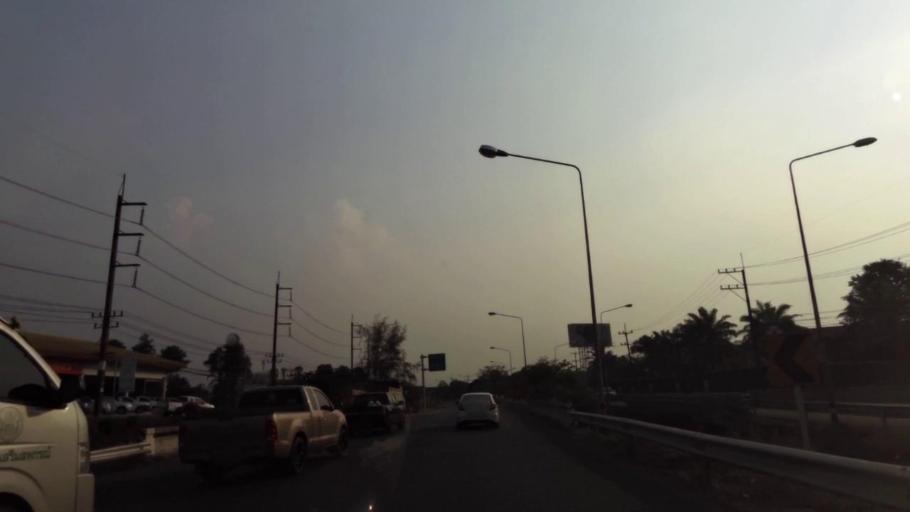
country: TH
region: Chanthaburi
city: Chanthaburi
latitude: 12.6071
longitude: 102.1338
